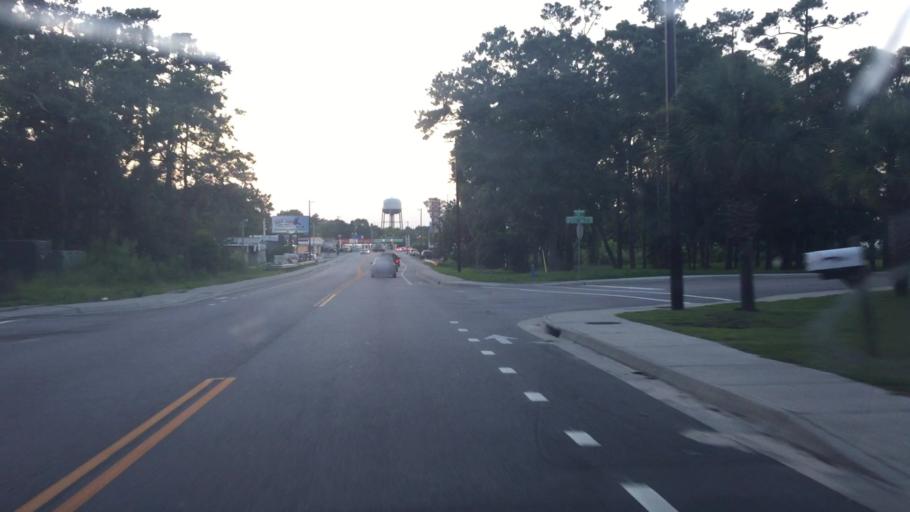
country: US
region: South Carolina
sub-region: Horry County
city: Myrtle Beach
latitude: 33.6877
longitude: -78.8941
